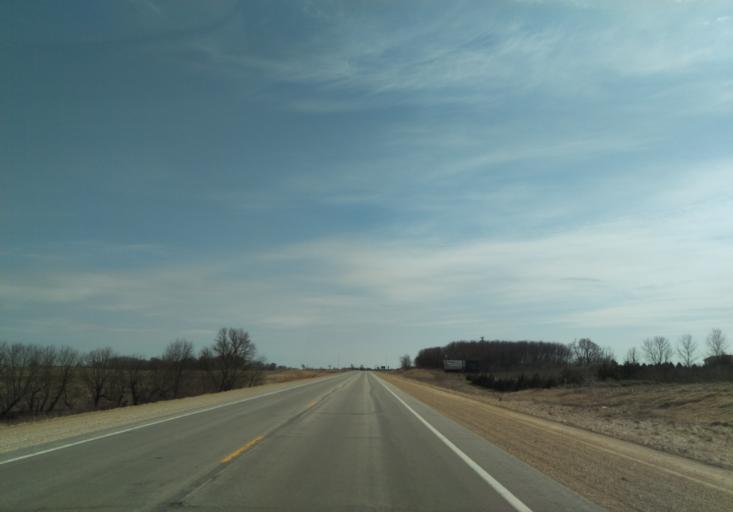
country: US
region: Iowa
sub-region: Winneshiek County
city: Decorah
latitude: 43.3719
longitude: -91.8111
